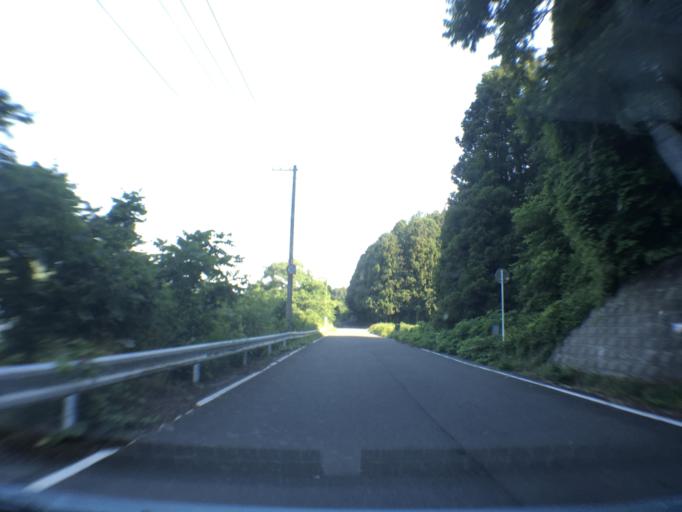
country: JP
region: Miyagi
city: Wakuya
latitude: 38.6260
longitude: 141.2900
